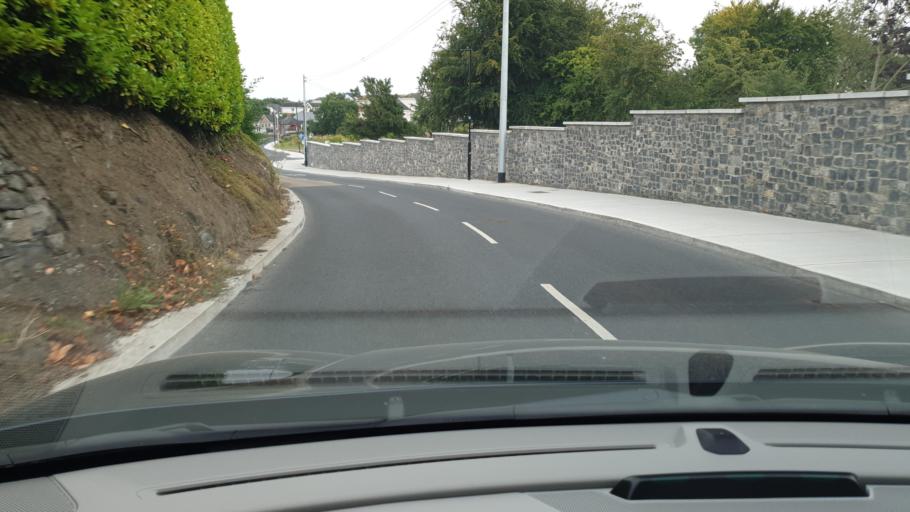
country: IE
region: Leinster
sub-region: An Mhi
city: Ashbourne
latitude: 53.5064
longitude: -6.3863
